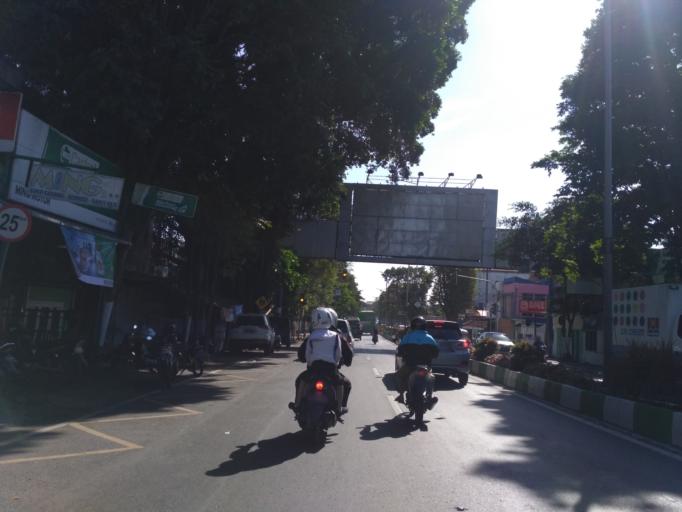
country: ID
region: East Java
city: Malang
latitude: -7.9380
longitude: 112.6439
